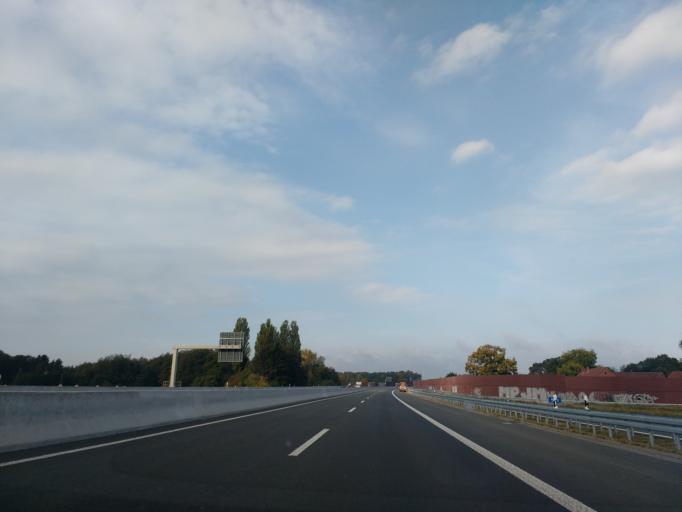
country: DE
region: North Rhine-Westphalia
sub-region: Regierungsbezirk Detmold
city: Bielefeld
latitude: 51.9736
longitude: 8.4783
